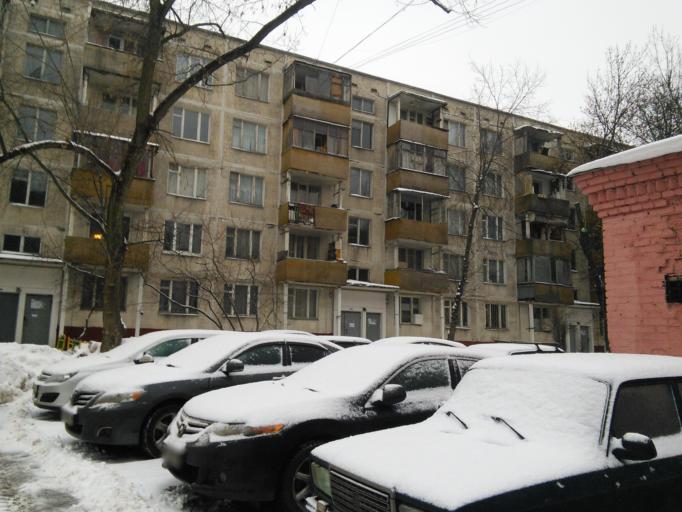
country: RU
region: Moscow
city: Lefortovo
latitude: 55.7699
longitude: 37.7113
